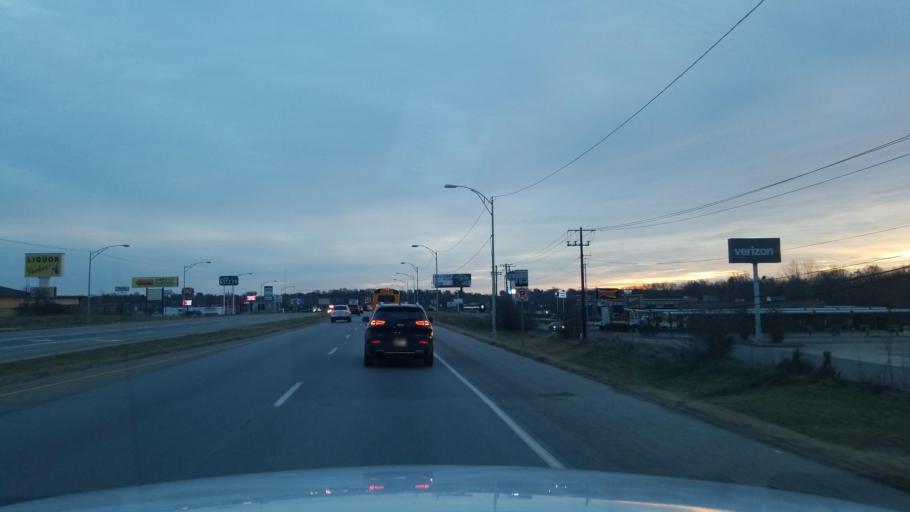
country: US
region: Indiana
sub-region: Vanderburgh County
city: Evansville
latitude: 37.9765
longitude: -87.6366
